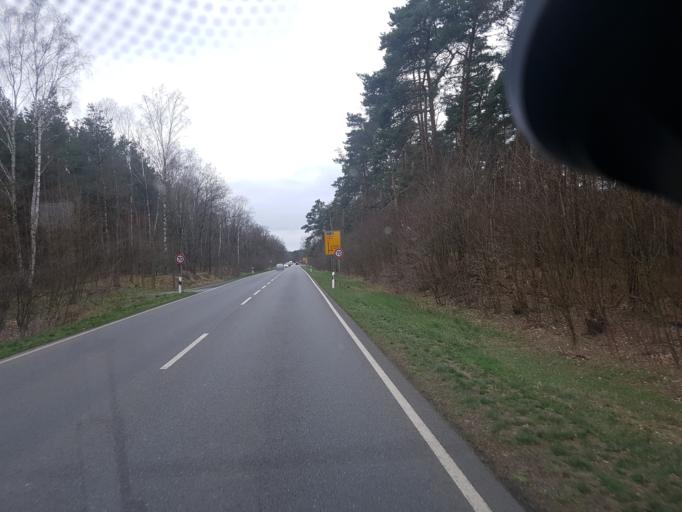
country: DE
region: Brandenburg
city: Luebben
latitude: 51.9585
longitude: 13.9343
